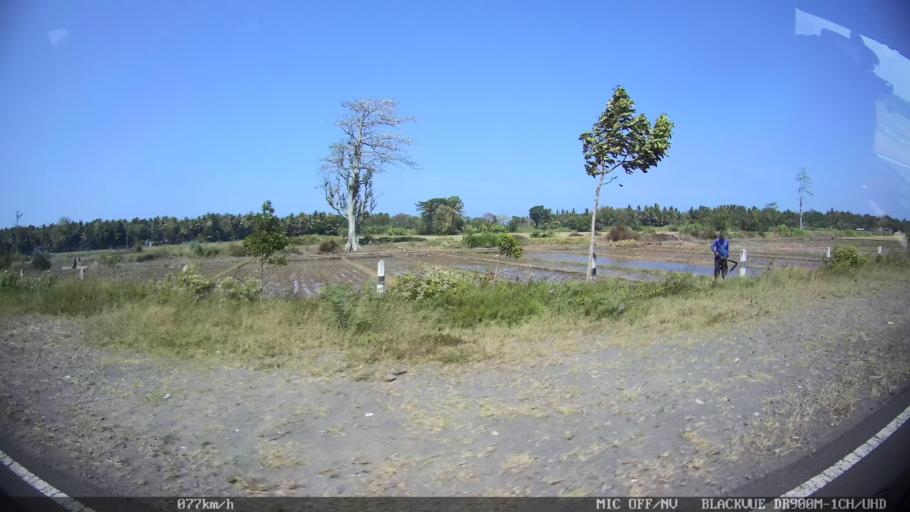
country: ID
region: Daerah Istimewa Yogyakarta
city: Srandakan
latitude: -7.9570
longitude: 110.1995
